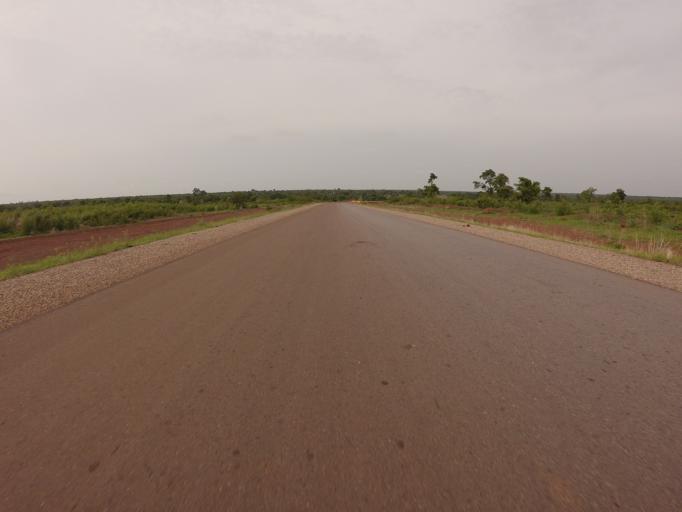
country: GH
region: Northern
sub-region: Yendi
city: Yendi
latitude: 9.7990
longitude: -0.1131
